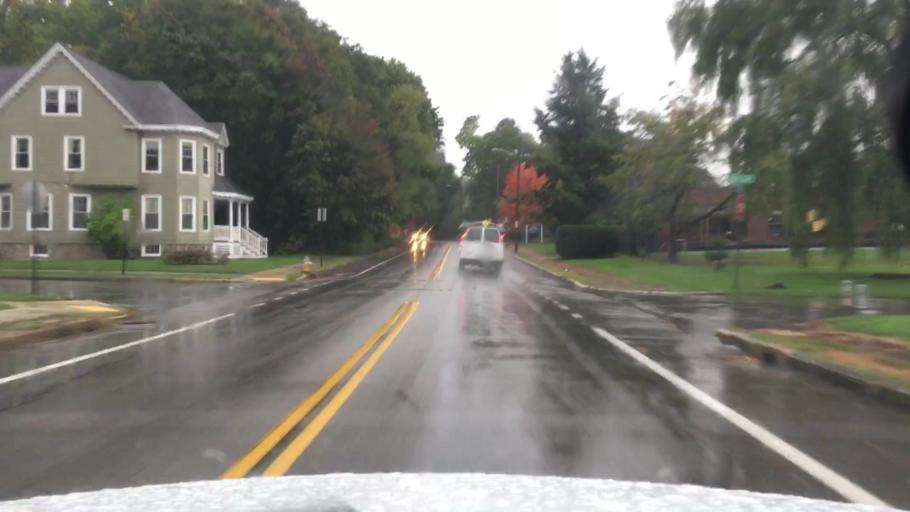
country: US
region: Maine
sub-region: Cumberland County
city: Portland
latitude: 43.6665
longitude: -70.2837
